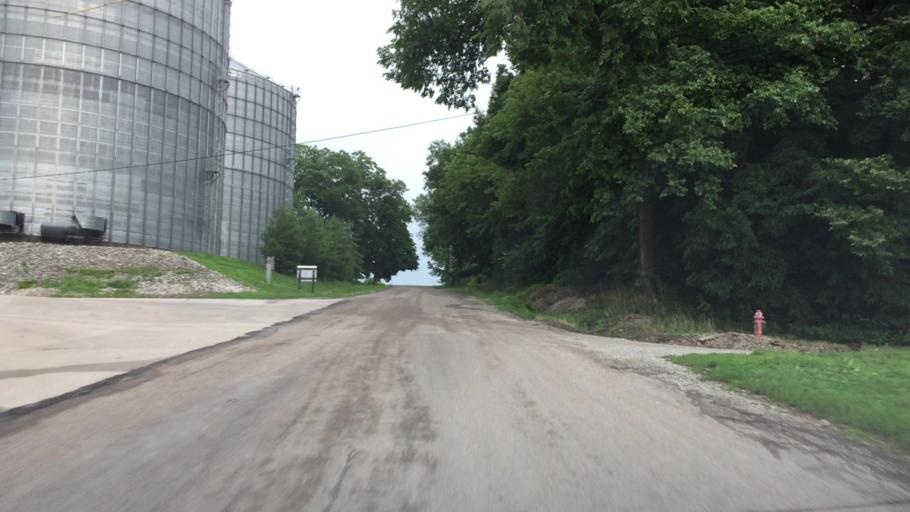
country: US
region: Illinois
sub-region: Hancock County
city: Warsaw
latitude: 40.3616
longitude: -91.4416
